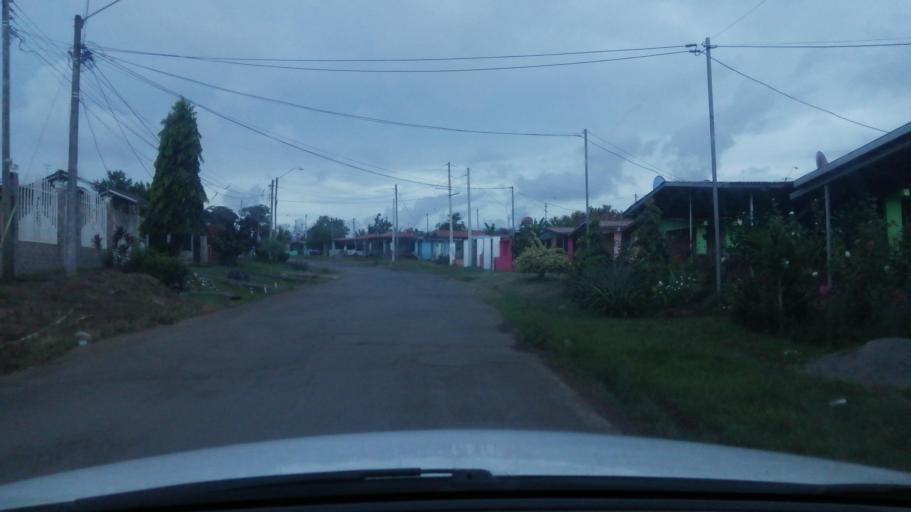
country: PA
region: Chiriqui
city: David
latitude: 8.4010
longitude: -82.4448
